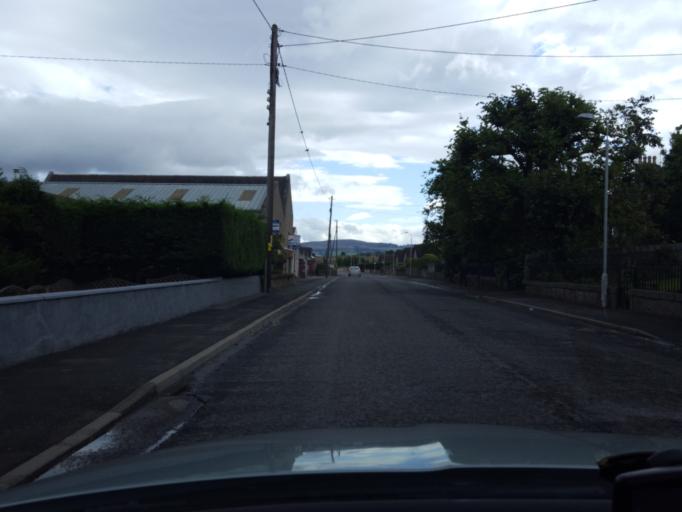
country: GB
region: Scotland
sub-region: Aberdeenshire
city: Alford
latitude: 57.2311
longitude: -2.6970
